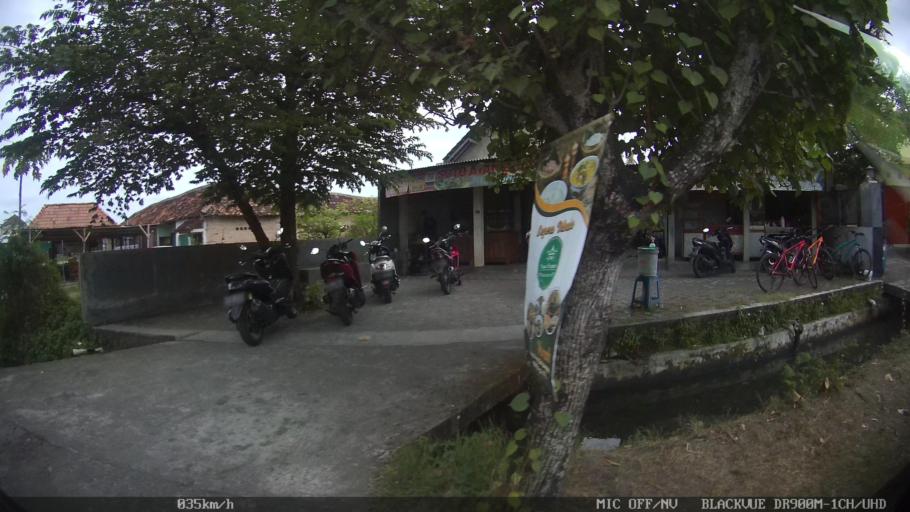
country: ID
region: Daerah Istimewa Yogyakarta
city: Sewon
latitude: -7.8364
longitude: 110.4164
